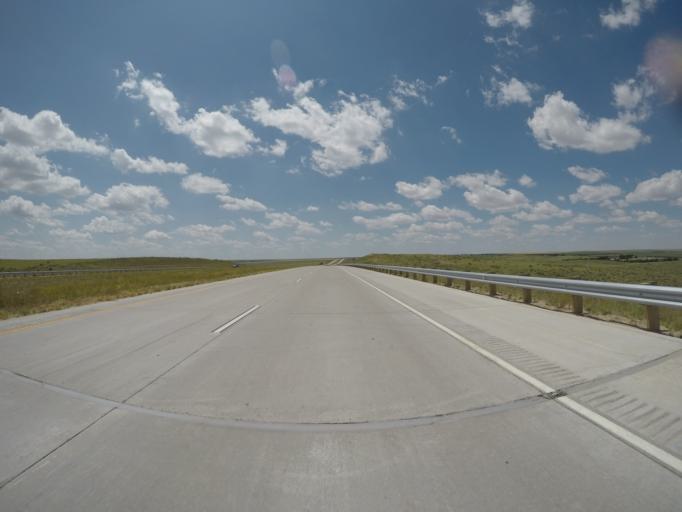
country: US
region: Colorado
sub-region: Kit Carson County
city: Burlington
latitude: 39.2942
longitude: -102.6401
